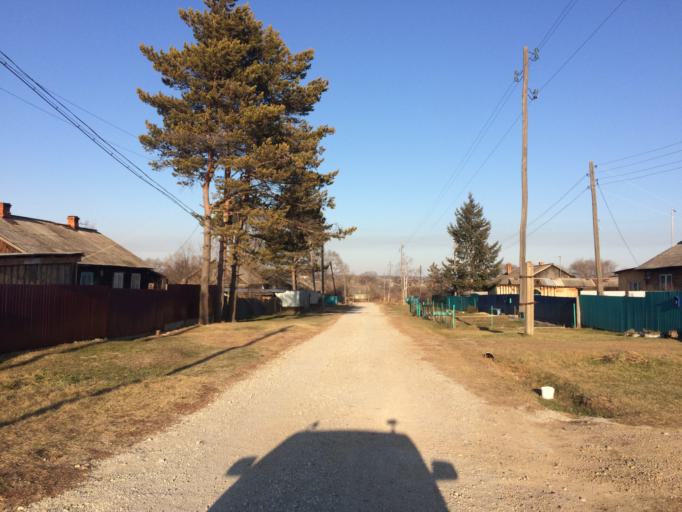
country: RU
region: Primorskiy
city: Ivanovka
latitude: 43.9557
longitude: 132.4699
